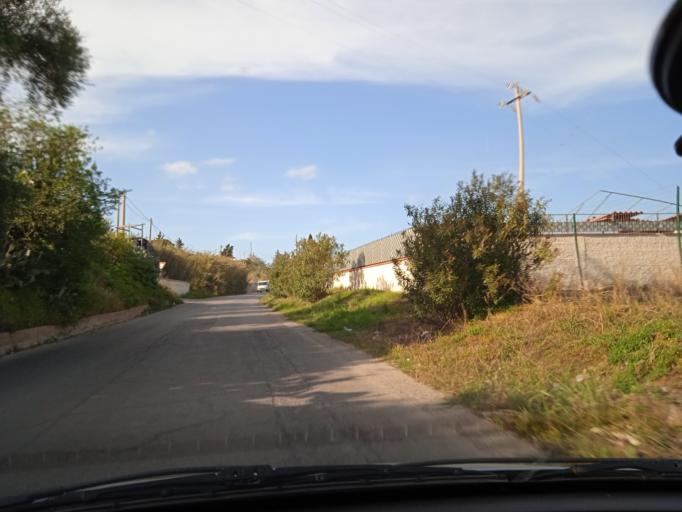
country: IT
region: Sicily
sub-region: Palermo
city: Portella di Mare
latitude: 38.0533
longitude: 13.4614
